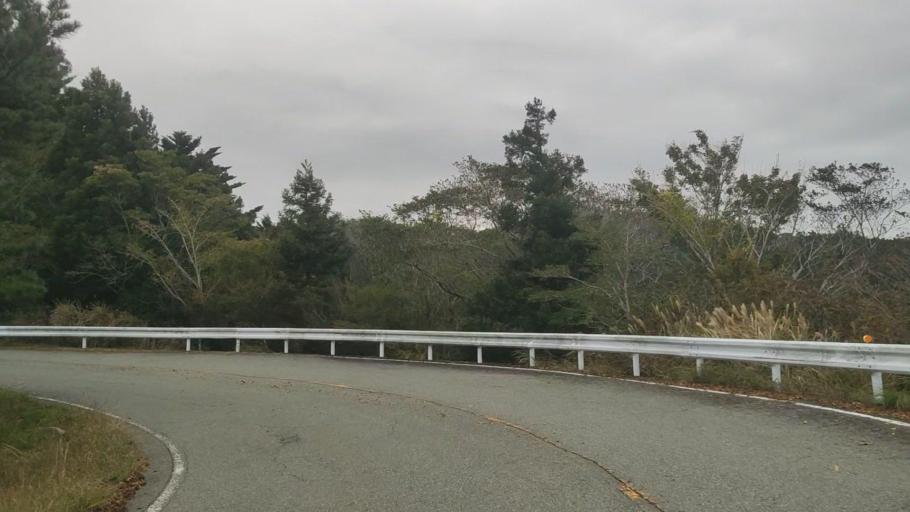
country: JP
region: Shizuoka
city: Heda
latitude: 34.9256
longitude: 138.8412
